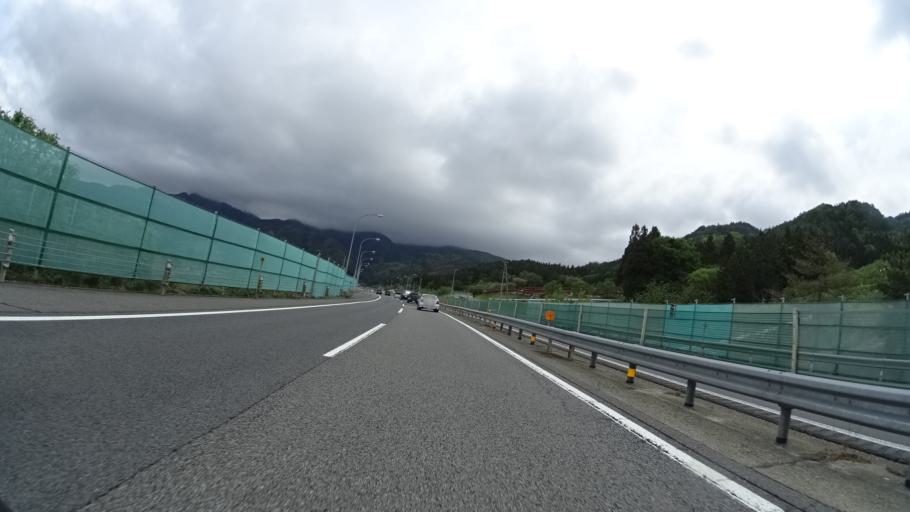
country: JP
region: Nagano
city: Nagano-shi
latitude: 36.5271
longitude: 138.0800
